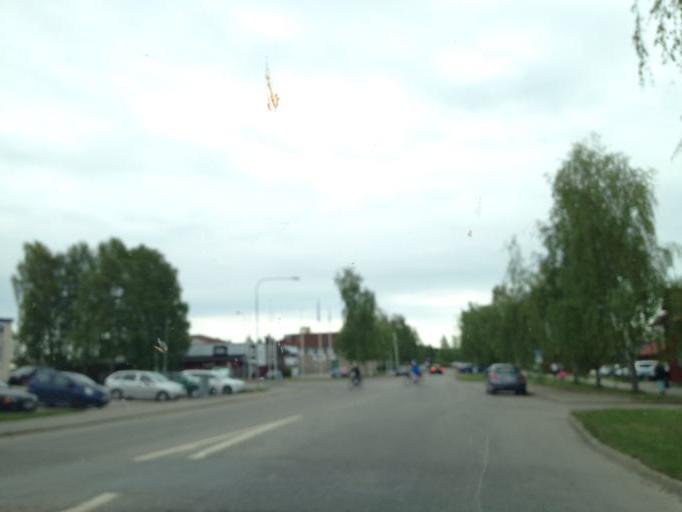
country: SE
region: Soedermanland
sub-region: Nykopings Kommun
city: Nykoping
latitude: 58.7473
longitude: 17.0181
